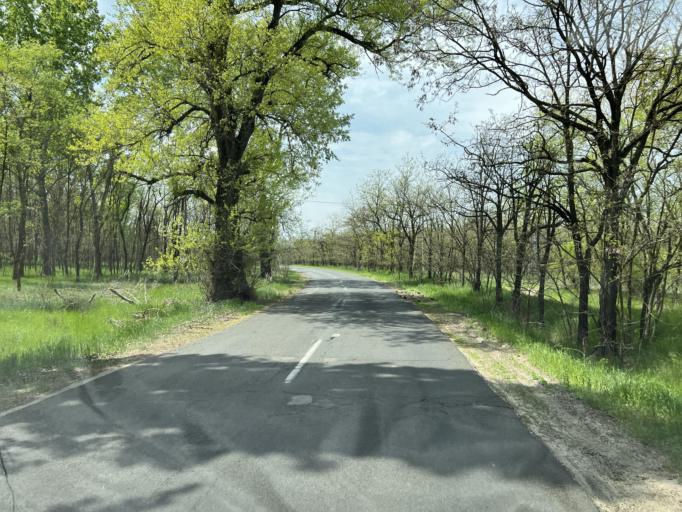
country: HU
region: Pest
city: Csemo
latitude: 47.1302
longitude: 19.6624
